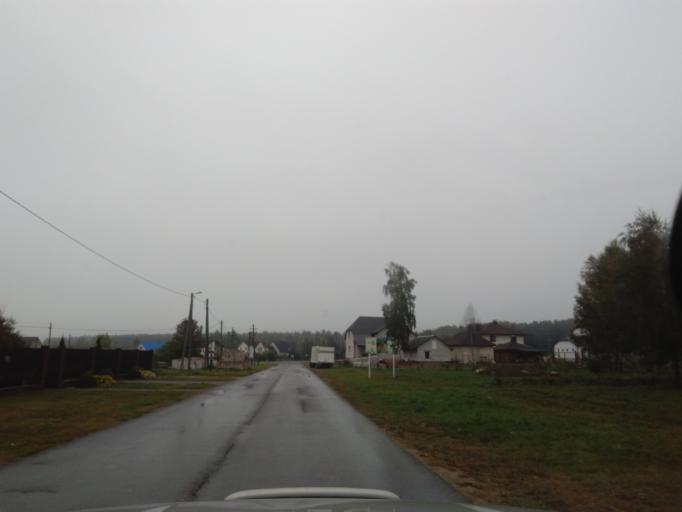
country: BY
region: Minsk
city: Kapyl'
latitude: 53.1565
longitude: 27.0988
